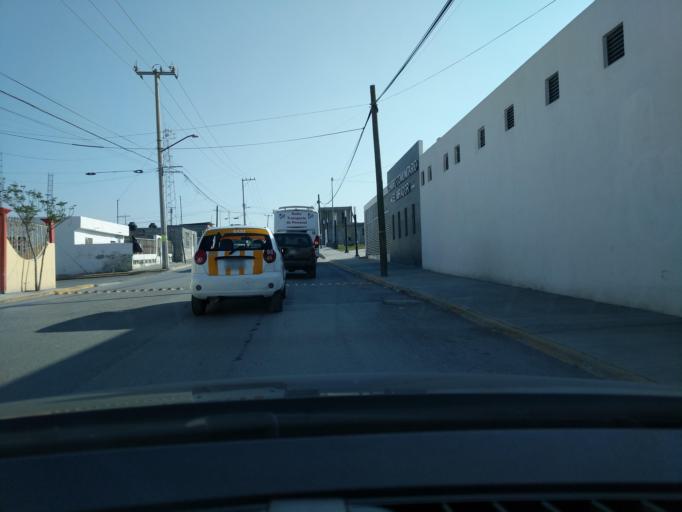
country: MX
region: Coahuila
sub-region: Ramos Arizpe
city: Ramos Arizpe
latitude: 25.5587
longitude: -100.9603
